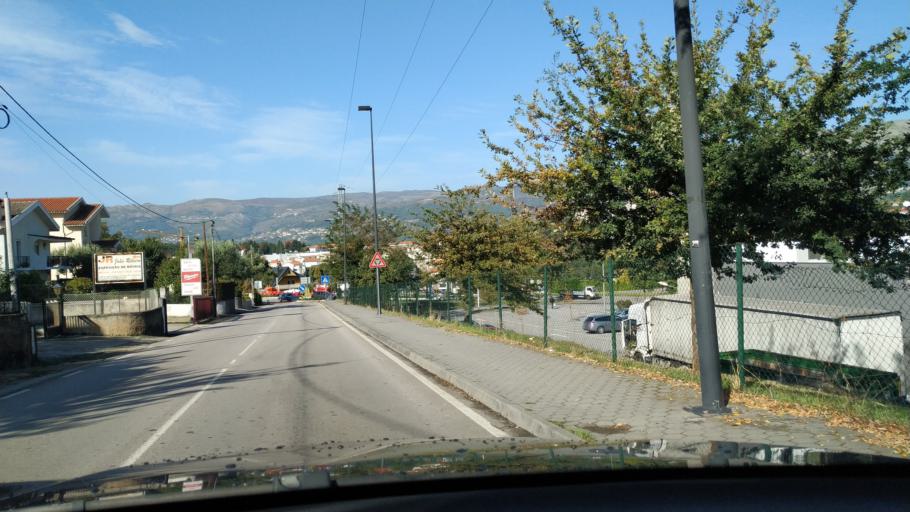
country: PT
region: Vila Real
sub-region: Vila Real
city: Vila Real
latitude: 41.3093
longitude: -7.7235
